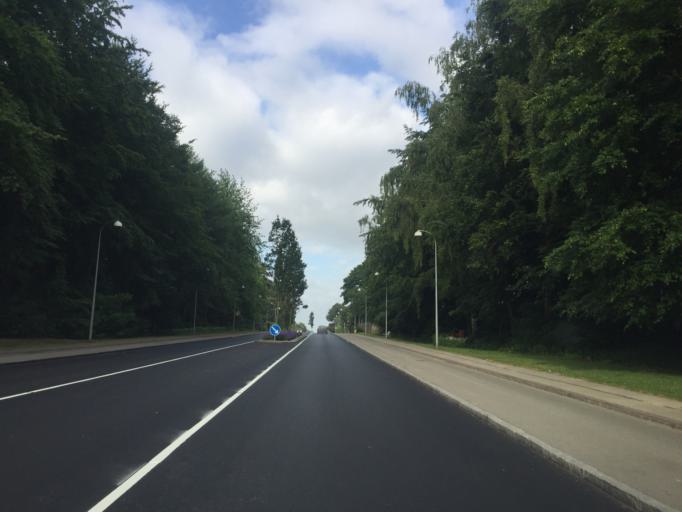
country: DK
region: Capital Region
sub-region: Brondby Kommune
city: Brondbyvester
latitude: 55.6557
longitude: 12.4358
